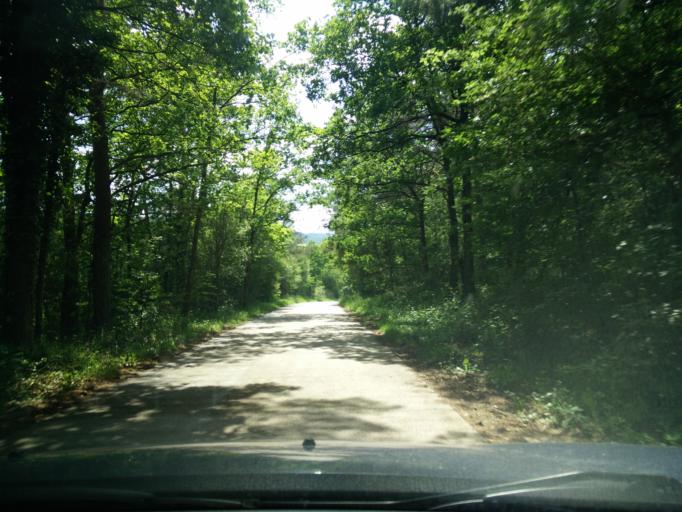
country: BE
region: Wallonia
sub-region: Province de Namur
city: Couvin
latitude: 50.0770
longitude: 4.6034
